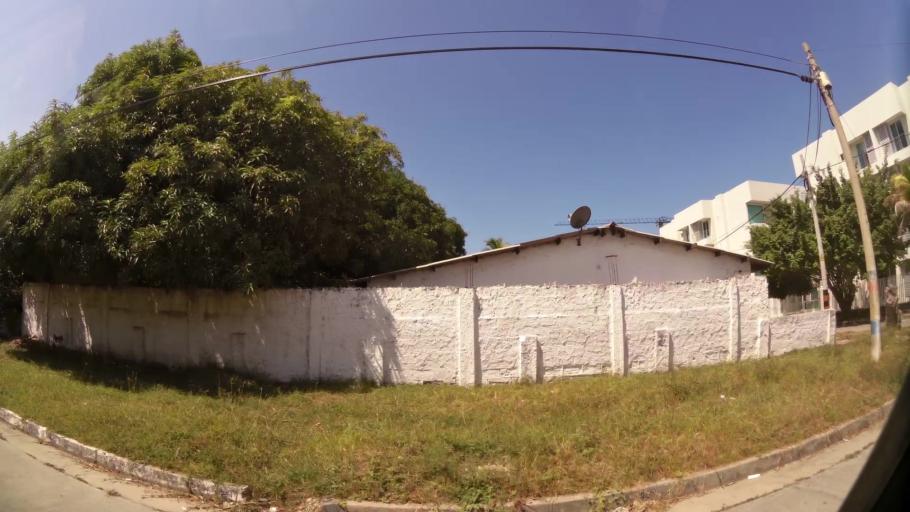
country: CO
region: Bolivar
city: Cartagena
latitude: 10.4491
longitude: -75.5160
